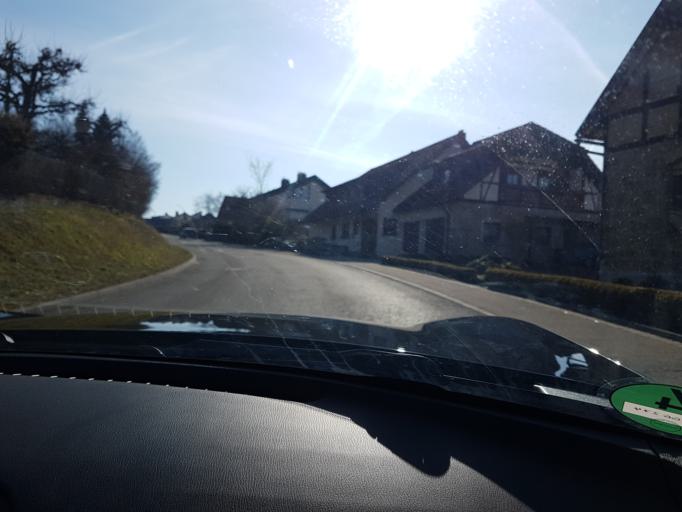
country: DE
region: Baden-Wuerttemberg
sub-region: Regierungsbezirk Stuttgart
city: Mulfingen
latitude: 49.3397
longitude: 9.8011
